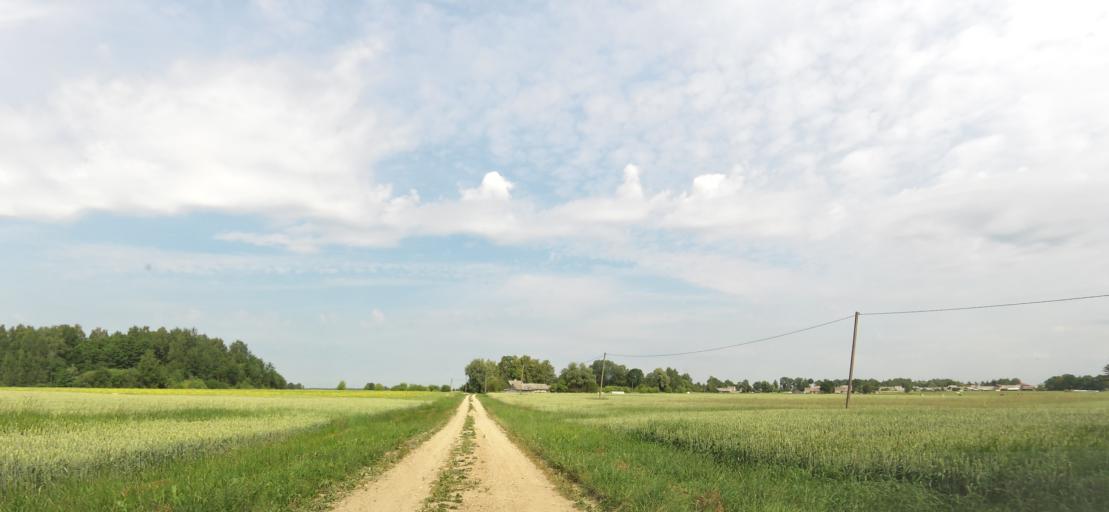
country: LT
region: Panevezys
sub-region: Birzai
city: Birzai
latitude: 56.3210
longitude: 24.6999
